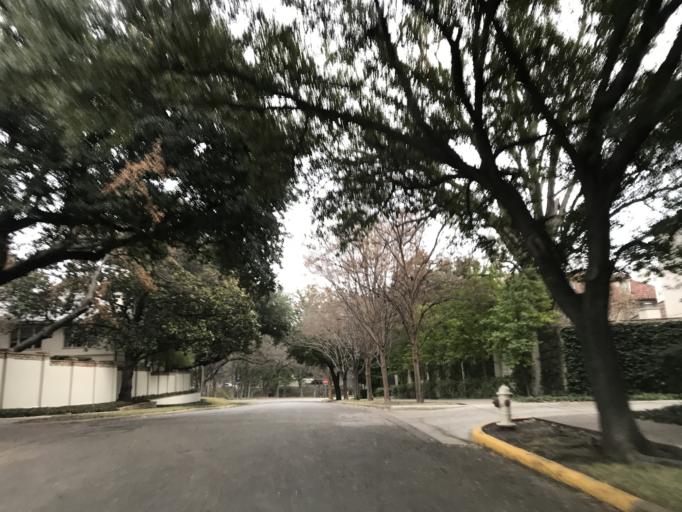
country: US
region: Texas
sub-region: Dallas County
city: Highland Park
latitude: 32.8248
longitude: -96.7995
